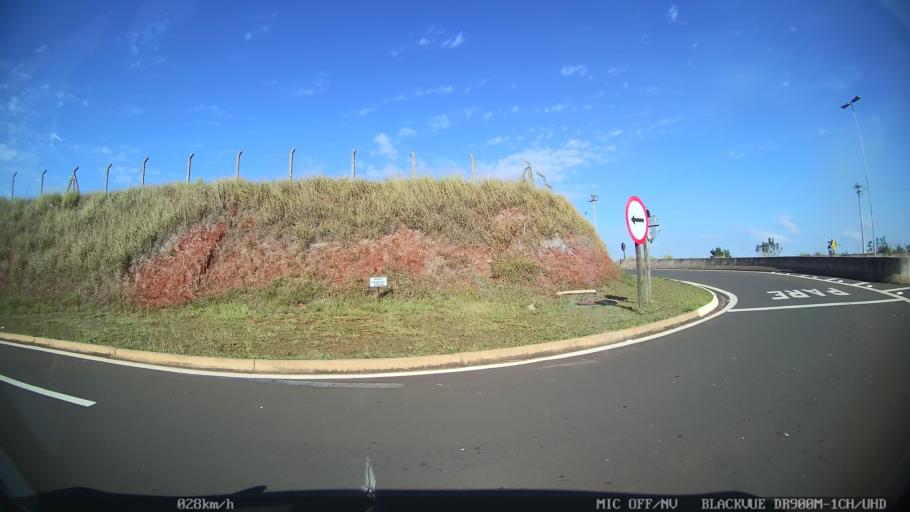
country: BR
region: Sao Paulo
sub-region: Piracicaba
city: Piracicaba
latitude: -22.6792
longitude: -47.5646
